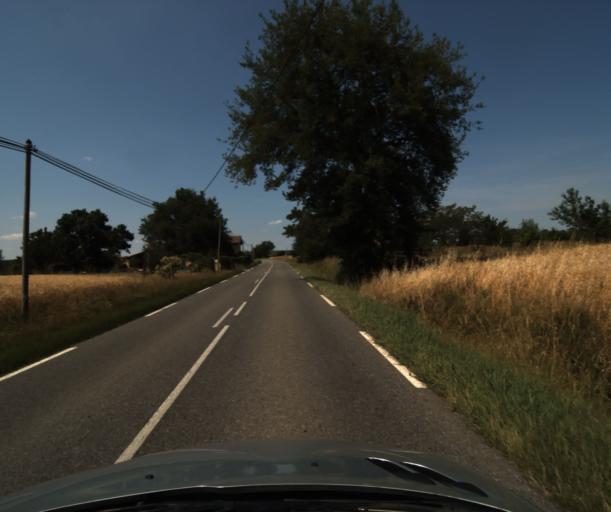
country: FR
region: Midi-Pyrenees
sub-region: Departement de la Haute-Garonne
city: Saint-Lys
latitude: 43.5271
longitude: 1.1722
